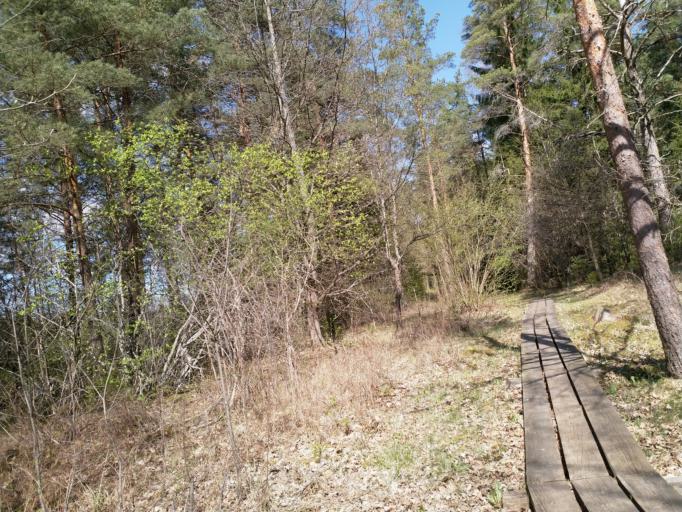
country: LV
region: Kandava
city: Kandava
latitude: 57.0188
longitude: 22.7727
